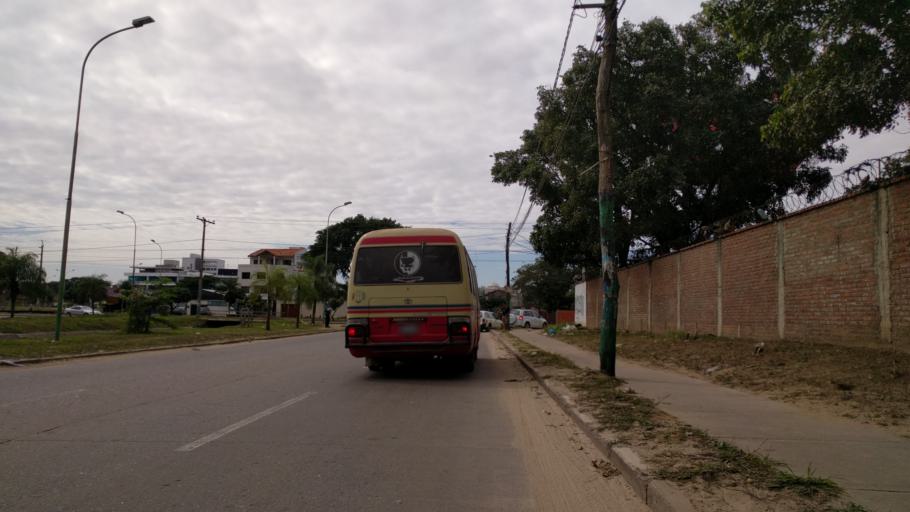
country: BO
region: Santa Cruz
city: Santa Cruz de la Sierra
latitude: -17.8065
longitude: -63.2133
